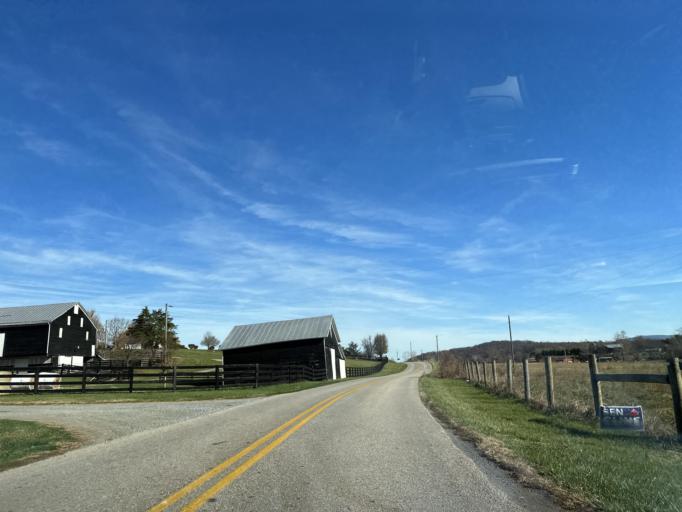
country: US
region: Virginia
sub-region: Augusta County
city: Fishersville
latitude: 38.1359
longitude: -78.9418
